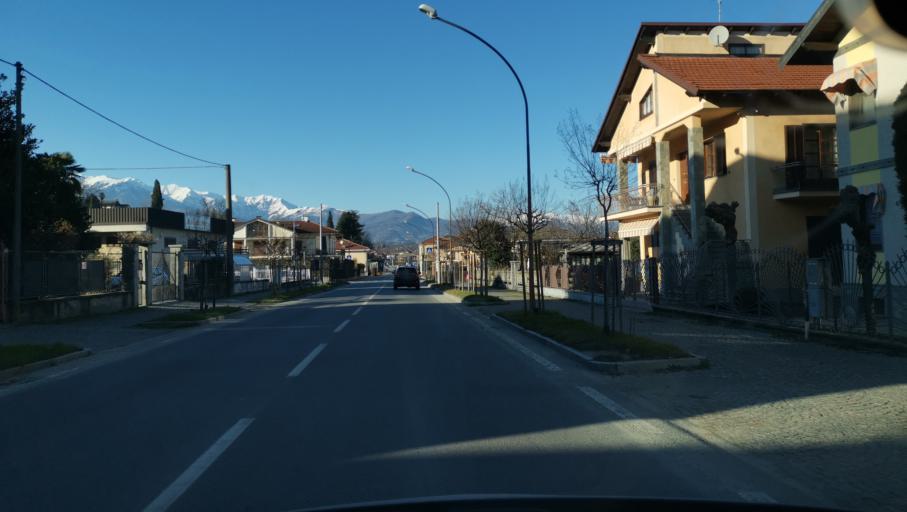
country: IT
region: Piedmont
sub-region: Provincia di Cuneo
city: Bagnolo Piemonte
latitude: 44.7630
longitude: 7.3136
